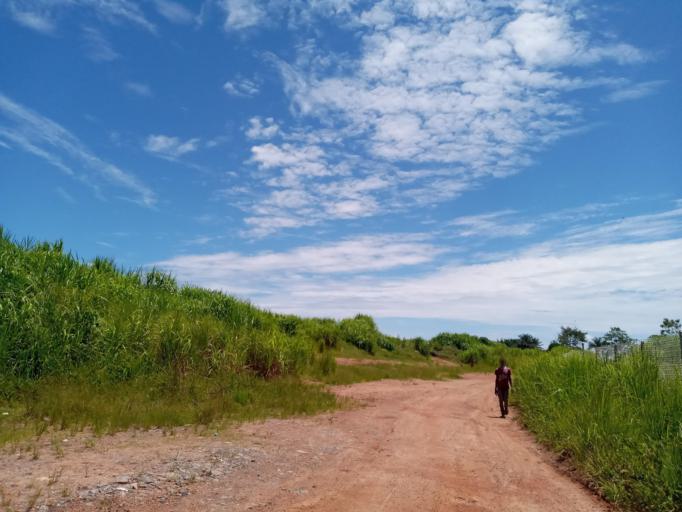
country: SL
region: Eastern Province
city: Koidu
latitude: 8.6540
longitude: -10.9488
